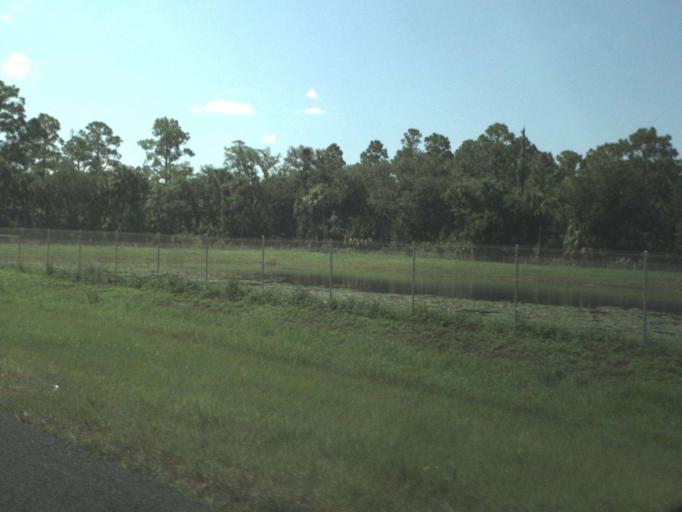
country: US
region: Florida
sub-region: Brevard County
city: Cocoa West
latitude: 28.3843
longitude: -80.9257
